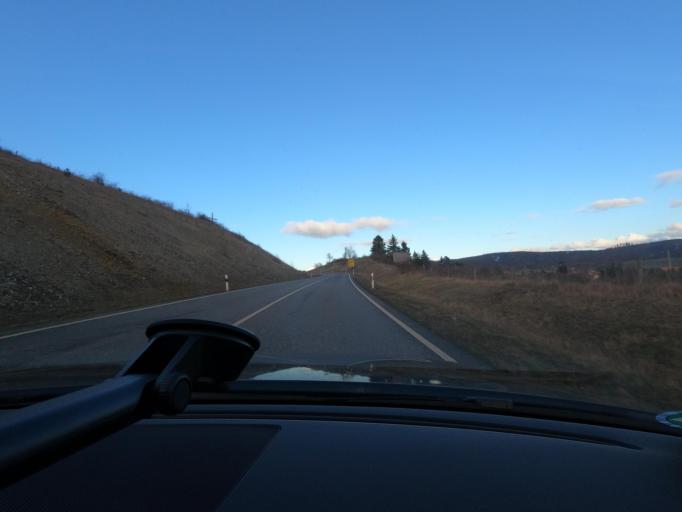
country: DE
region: Thuringia
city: Worbis
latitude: 51.4153
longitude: 10.3557
